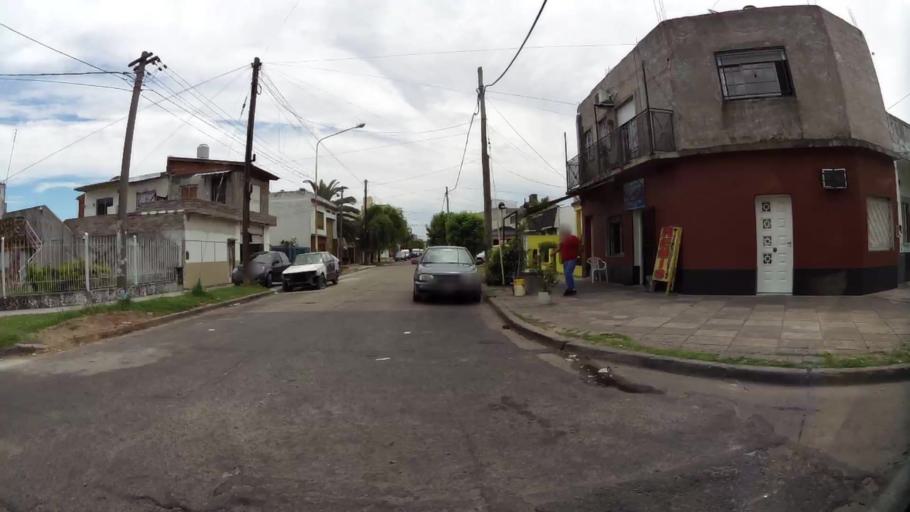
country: AR
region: Buenos Aires
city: San Justo
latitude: -34.6692
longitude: -58.5443
